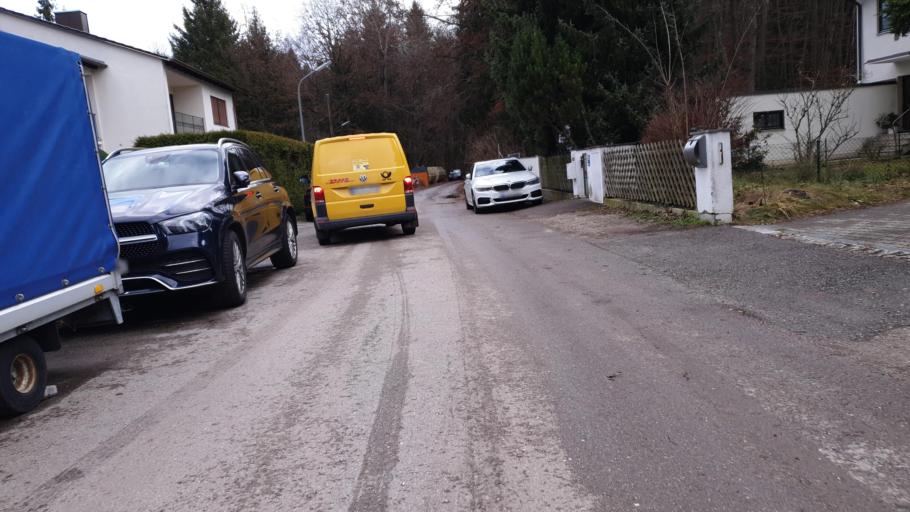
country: DE
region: Bavaria
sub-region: Upper Bavaria
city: Grobenzell
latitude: 48.1715
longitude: 11.3874
